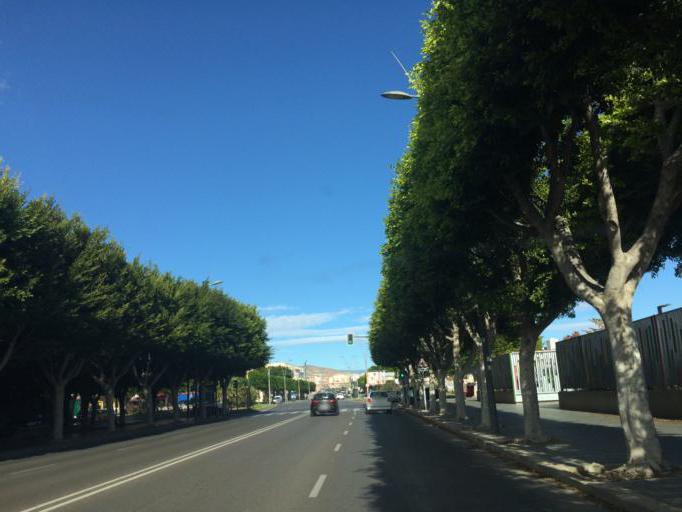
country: ES
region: Andalusia
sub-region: Provincia de Almeria
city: Almeria
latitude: 36.8308
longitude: -2.4460
